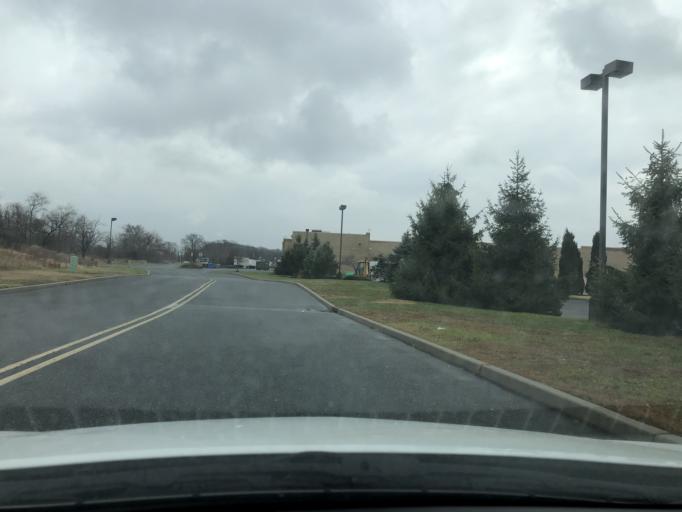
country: US
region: New Jersey
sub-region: Camden County
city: Glendora
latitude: 39.8413
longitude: -75.0900
